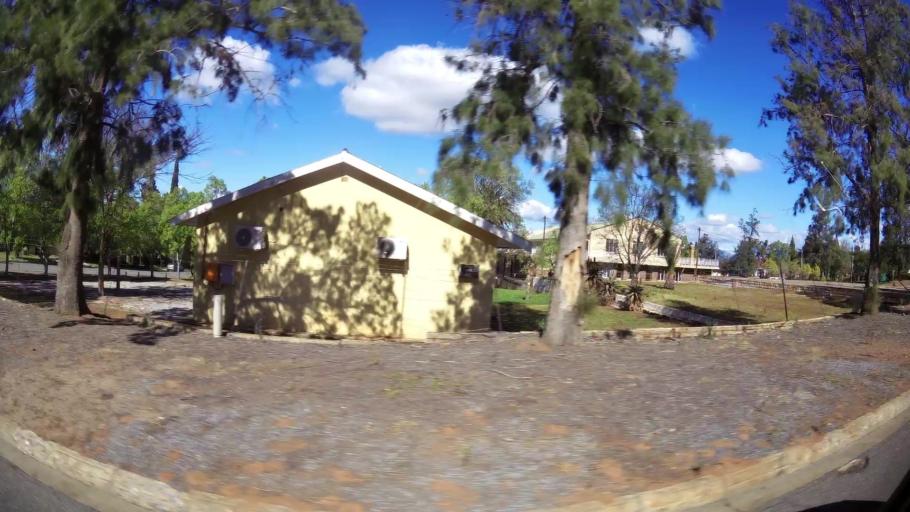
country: ZA
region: Western Cape
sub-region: Cape Winelands District Municipality
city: Ashton
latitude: -33.8313
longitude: 20.0557
